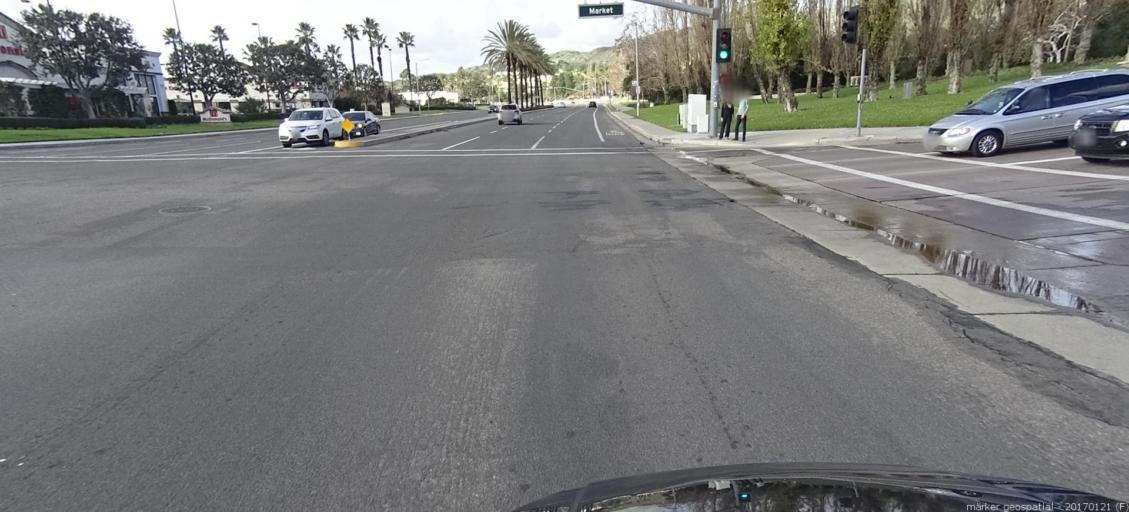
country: US
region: California
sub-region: Orange County
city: Foothill Ranch
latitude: 33.6803
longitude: -117.6646
